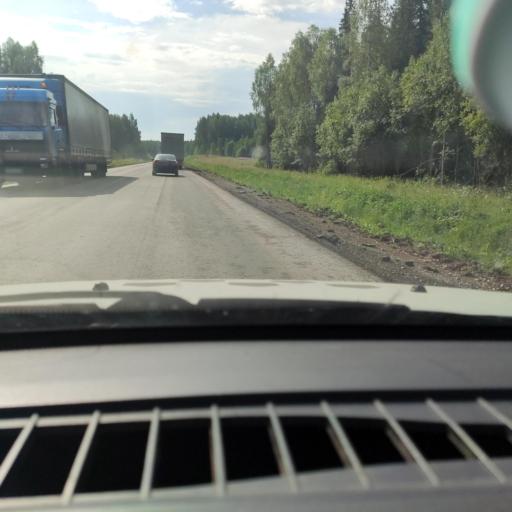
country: RU
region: Perm
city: Siva
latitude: 58.4537
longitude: 54.4160
